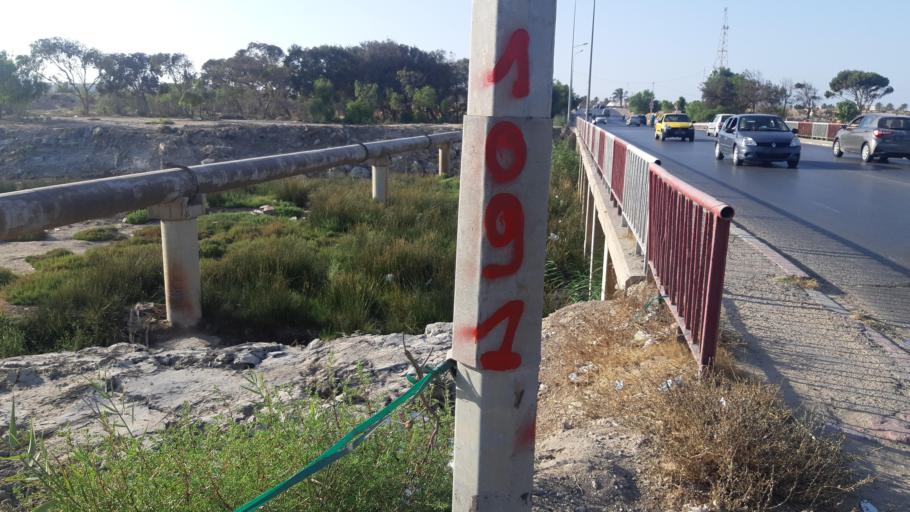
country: TN
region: Qabis
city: Gabes
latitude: 33.8778
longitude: 10.1102
